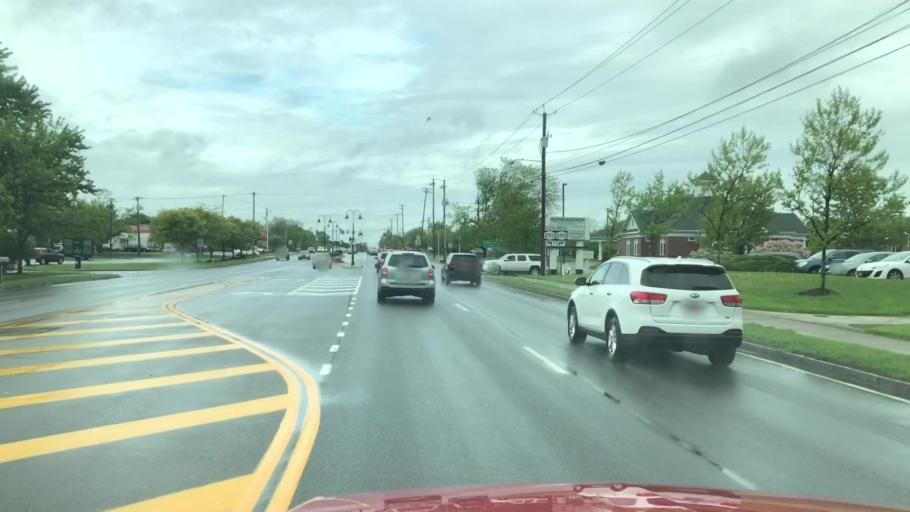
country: US
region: New York
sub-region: Monroe County
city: Fairport
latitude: 43.1308
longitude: -77.4384
